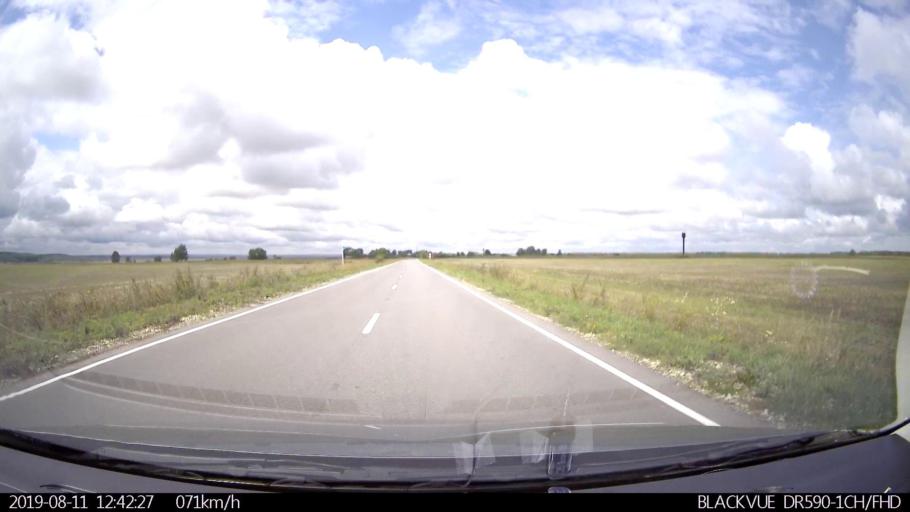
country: RU
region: Ulyanovsk
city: Ignatovka
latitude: 53.8459
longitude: 47.7514
